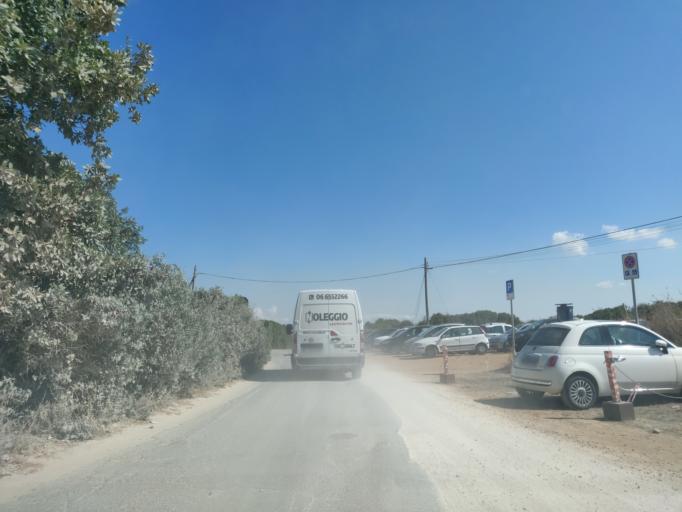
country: IT
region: Latium
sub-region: Citta metropolitana di Roma Capitale
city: Aurelia
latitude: 42.1696
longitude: 11.7411
